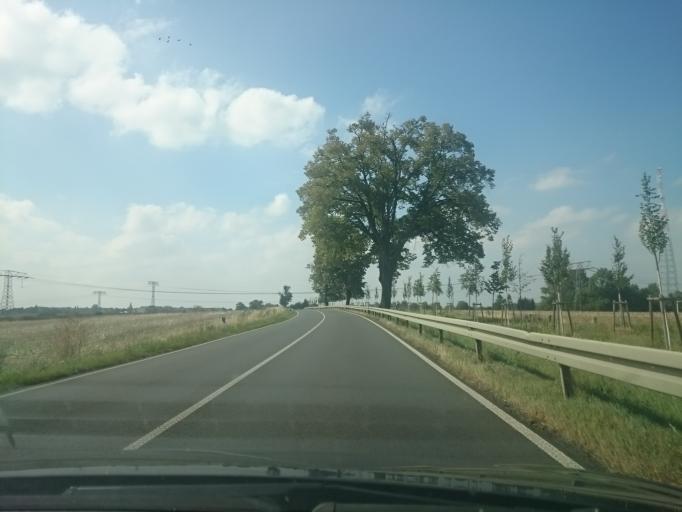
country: DE
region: Mecklenburg-Vorpommern
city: Viereck
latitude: 53.5050
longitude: 14.0359
